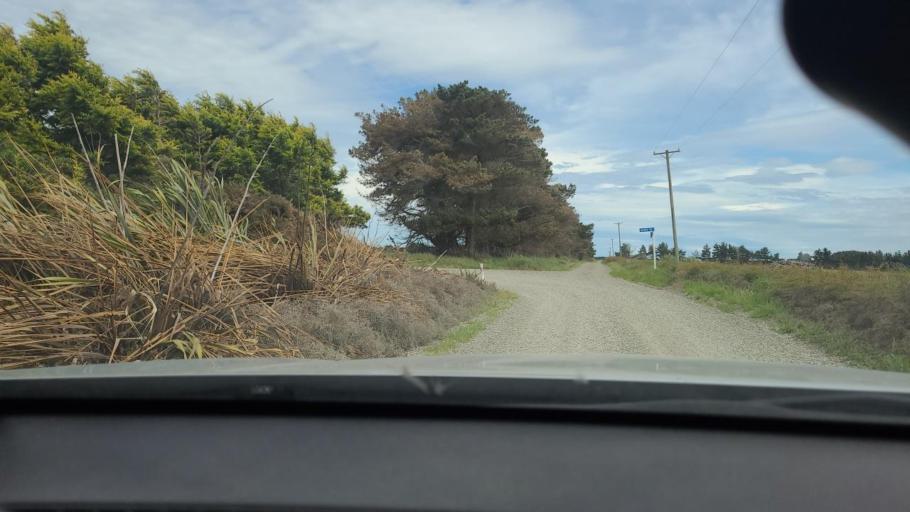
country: NZ
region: Southland
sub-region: Southland District
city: Riverton
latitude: -46.3452
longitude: 168.1822
